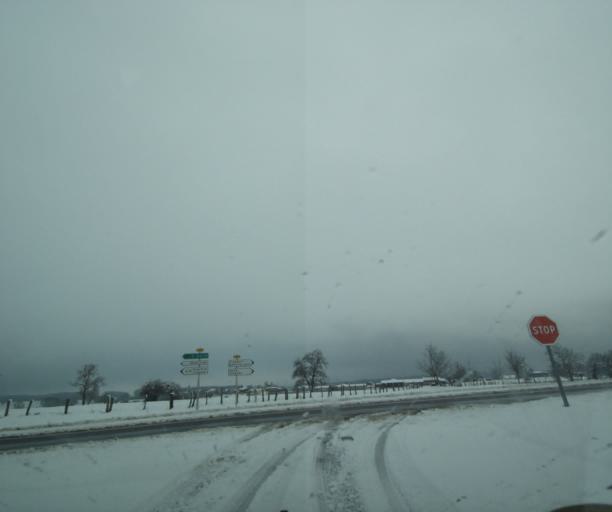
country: FR
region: Champagne-Ardenne
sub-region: Departement de la Haute-Marne
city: Montier-en-Der
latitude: 48.5224
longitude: 4.8113
